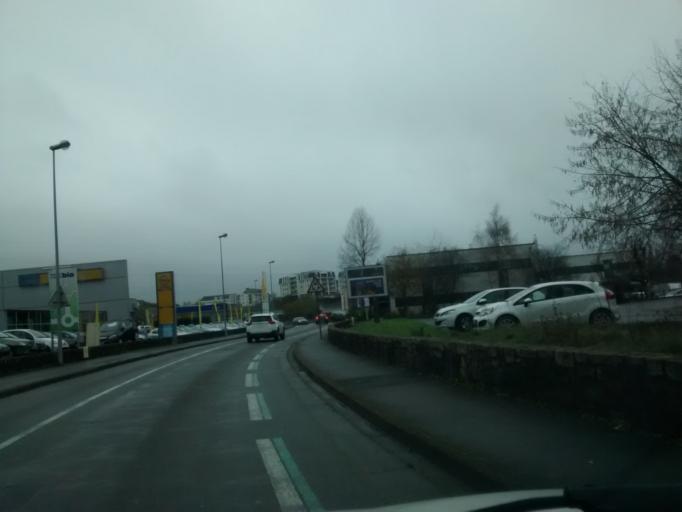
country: FR
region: Brittany
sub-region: Departement d'Ille-et-Vilaine
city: Cesson-Sevigne
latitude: 48.1138
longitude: -1.6075
